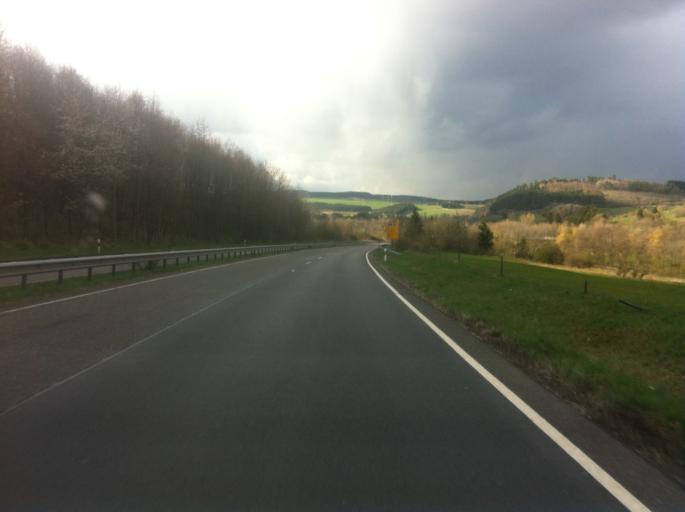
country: DE
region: Rheinland-Pfalz
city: Kerschenbach
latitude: 50.3567
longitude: 6.5116
